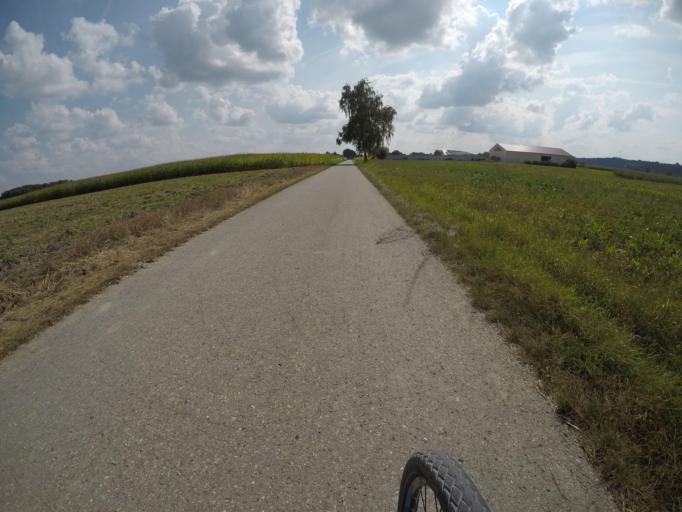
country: DE
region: Bavaria
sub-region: Swabia
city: Nordendorf
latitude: 48.5829
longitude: 10.8360
